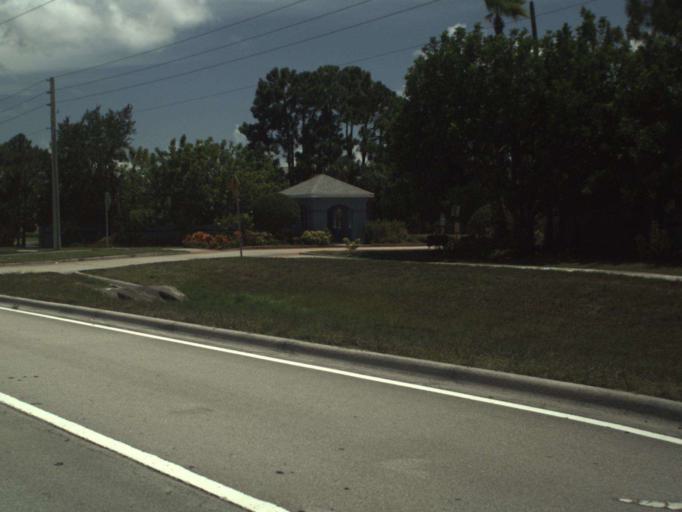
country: US
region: Florida
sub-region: Saint Lucie County
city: Port Saint Lucie
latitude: 27.2904
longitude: -80.2998
